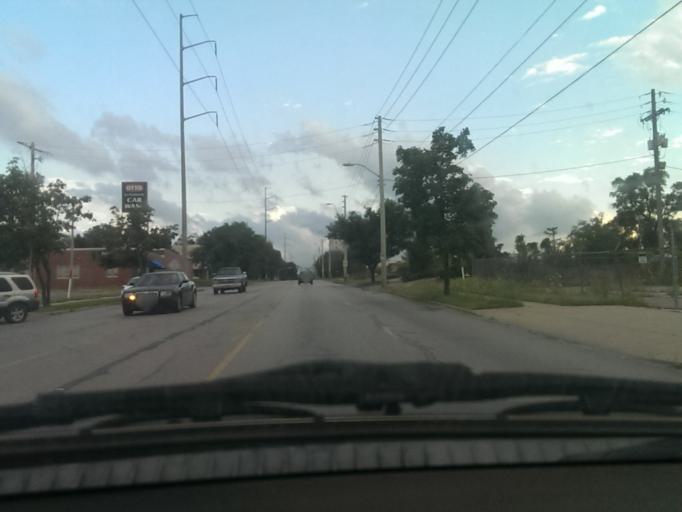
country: US
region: Kansas
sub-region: Johnson County
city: Mission Hills
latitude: 39.0092
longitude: -94.5748
